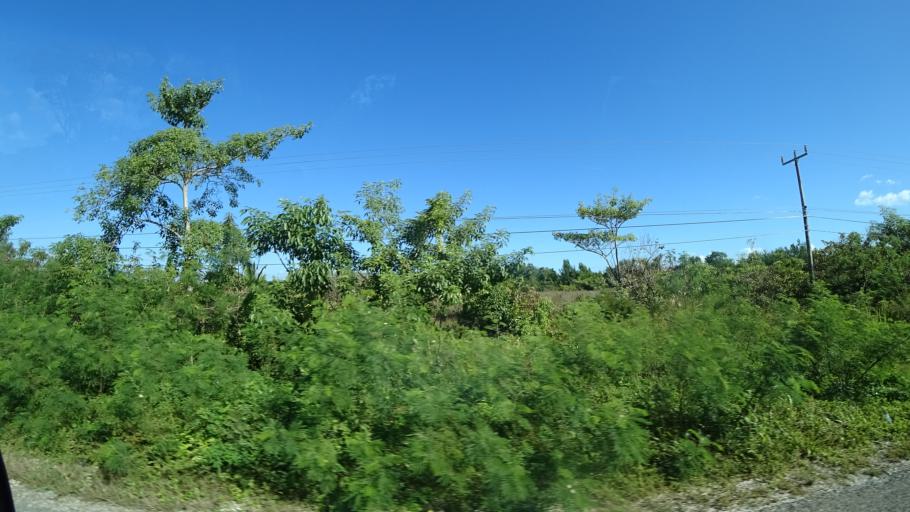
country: BZ
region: Belize
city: Belize City
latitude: 17.5455
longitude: -88.2741
